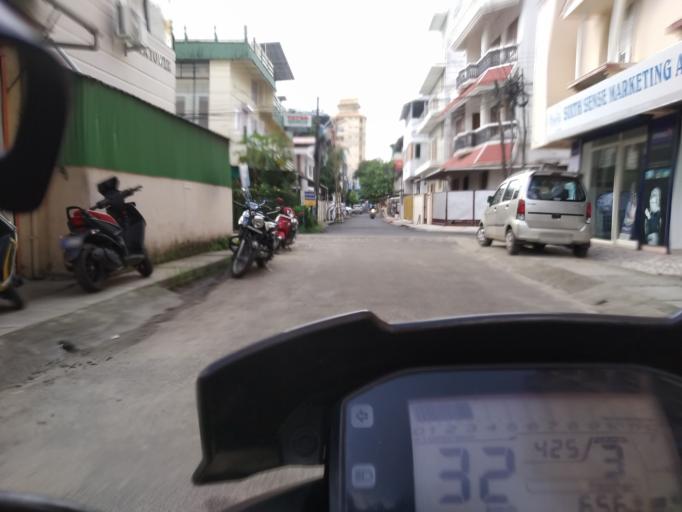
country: IN
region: Kerala
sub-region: Ernakulam
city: Cochin
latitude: 9.9898
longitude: 76.2805
